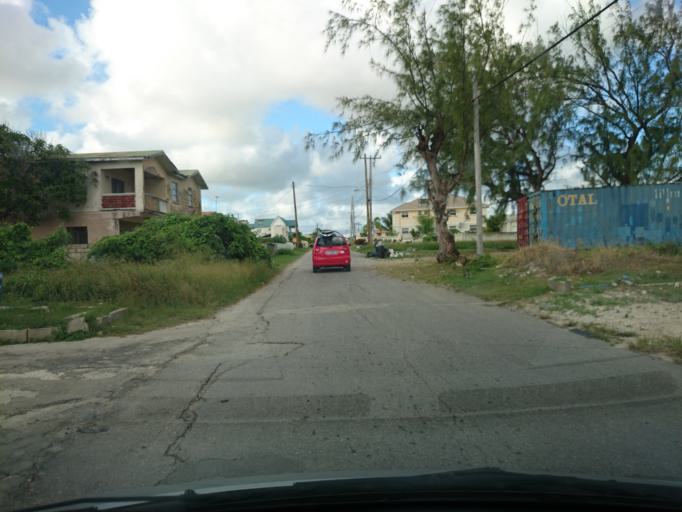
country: BB
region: Christ Church
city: Oistins
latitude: 13.0538
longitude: -59.5109
